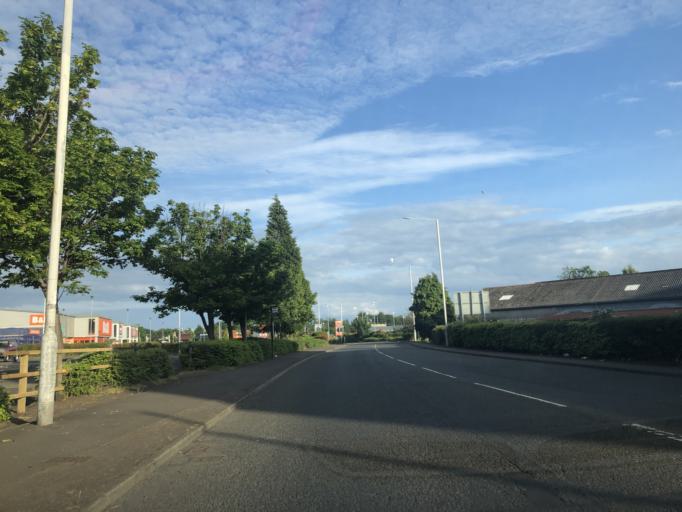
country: GB
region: Scotland
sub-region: Fife
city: Leven
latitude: 56.1958
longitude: -3.0044
